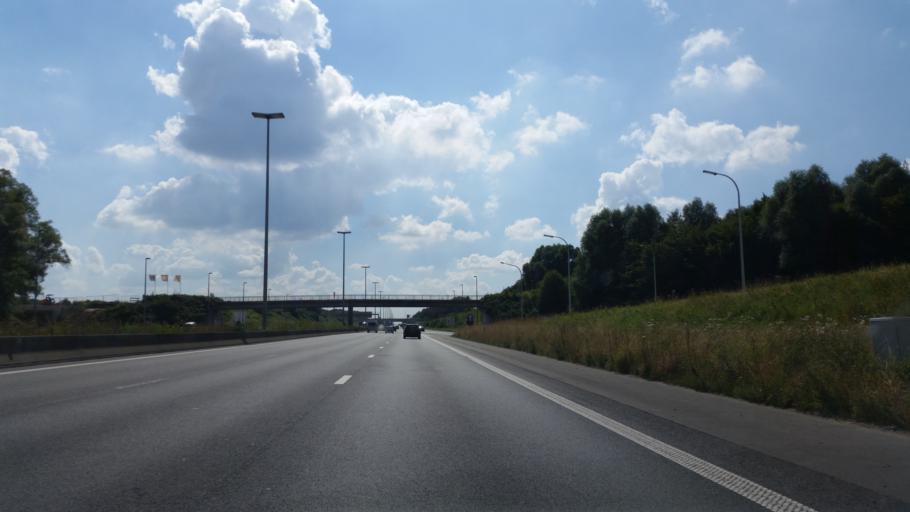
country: BE
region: Flanders
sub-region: Provincie West-Vlaanderen
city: Kortrijk
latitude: 50.8059
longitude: 3.2654
